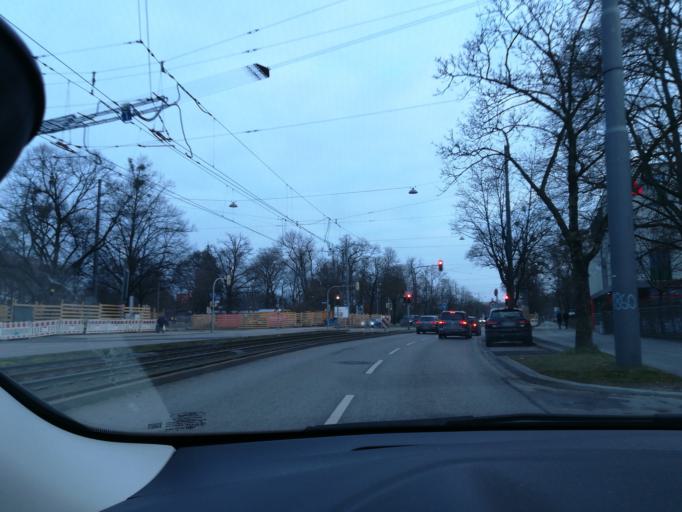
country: DE
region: Bavaria
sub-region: Upper Bavaria
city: Pasing
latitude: 48.1541
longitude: 11.5125
